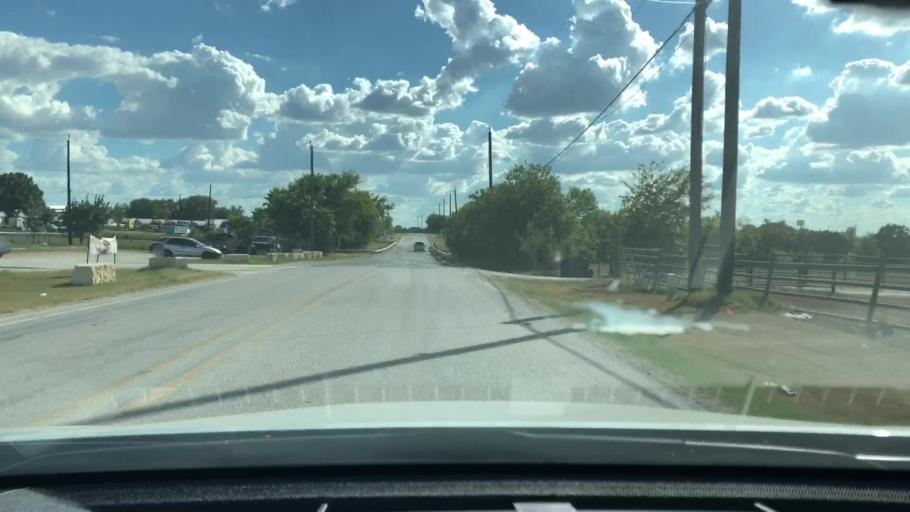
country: US
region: Texas
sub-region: Guadalupe County
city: Northcliff
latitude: 29.6292
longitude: -98.2477
